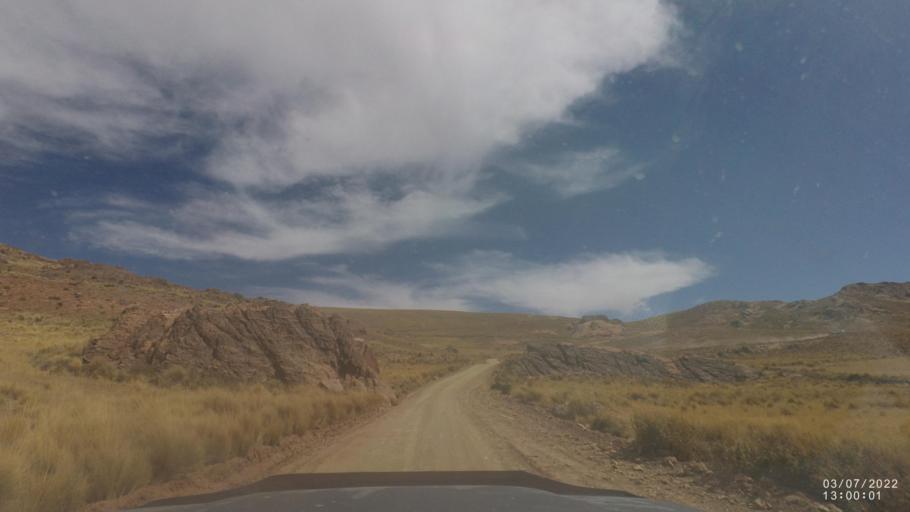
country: BO
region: Cochabamba
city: Colchani
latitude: -17.7148
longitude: -66.6874
